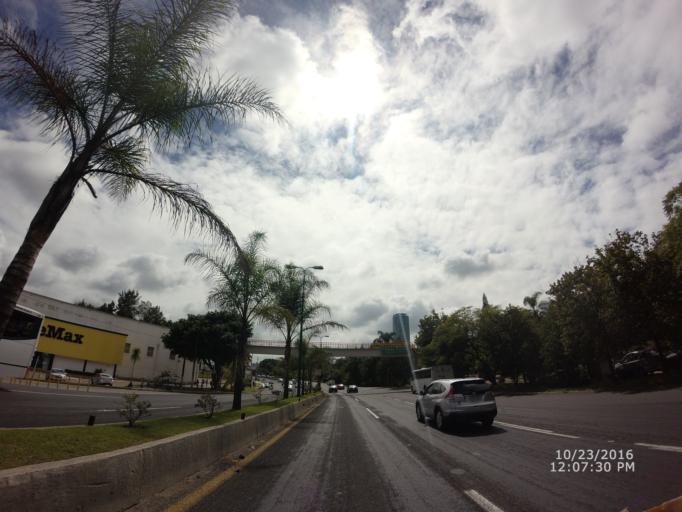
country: MX
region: Veracruz
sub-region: Xalapa
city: Lomas Verdes
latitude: 19.5191
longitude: -96.8833
